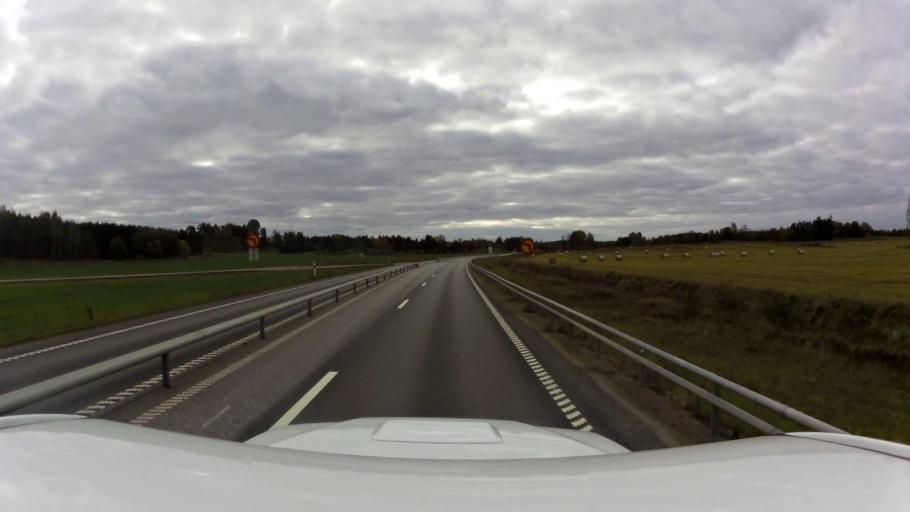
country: SE
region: OEstergoetland
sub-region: Linkopings Kommun
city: Malmslatt
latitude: 58.3230
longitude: 15.5670
